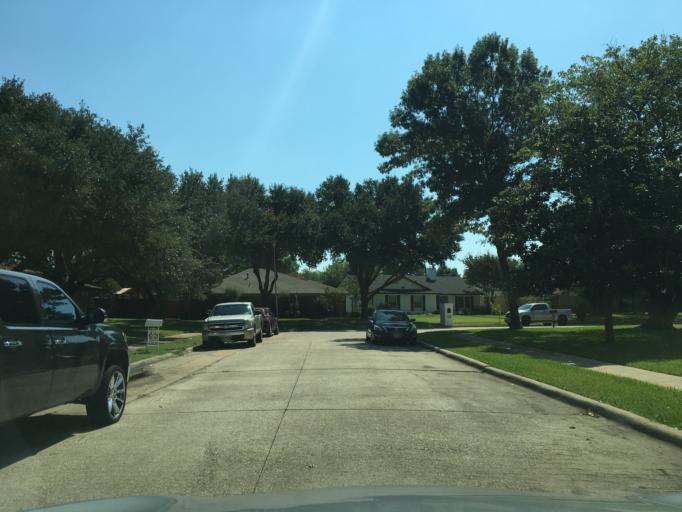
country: US
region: Texas
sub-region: Dallas County
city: Garland
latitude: 32.9375
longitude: -96.6593
